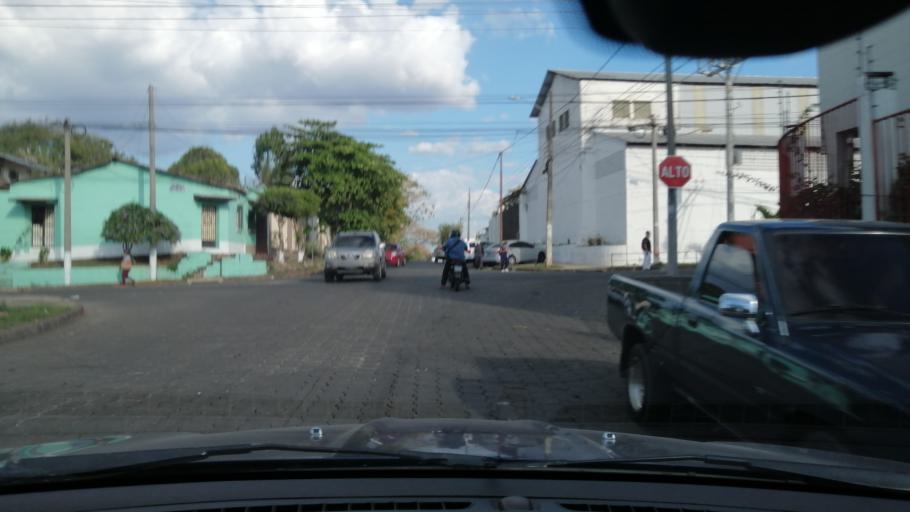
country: SV
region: Santa Ana
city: Santa Ana
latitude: 13.9837
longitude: -89.5609
